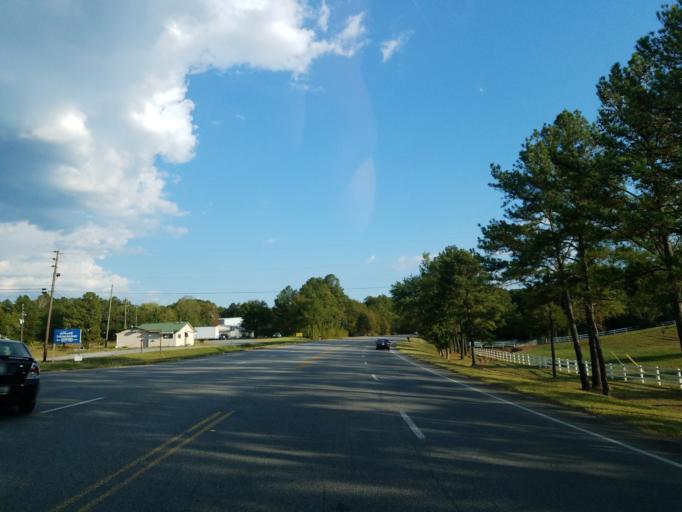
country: US
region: Georgia
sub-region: Murray County
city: Chatsworth
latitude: 34.7323
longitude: -84.7533
